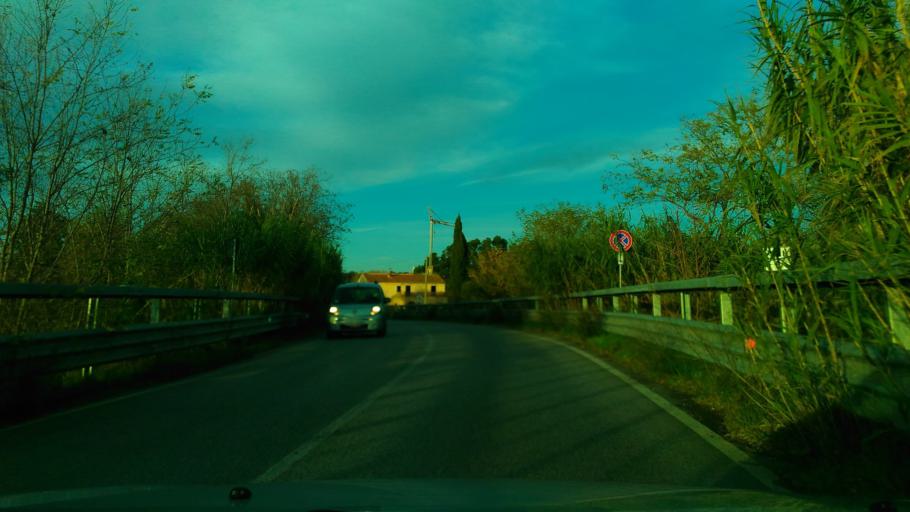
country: IT
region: Tuscany
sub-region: Provincia di Livorno
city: S.P. in Palazzi
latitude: 43.3600
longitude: 10.5102
